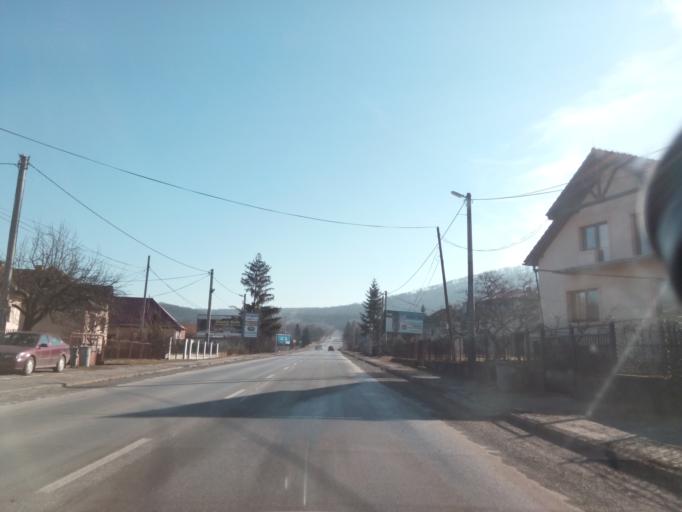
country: SK
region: Kosicky
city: Secovce
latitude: 48.7399
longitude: 21.5022
